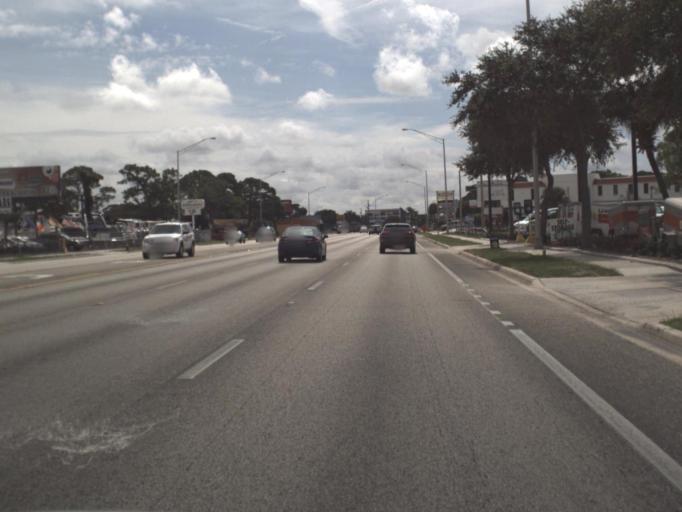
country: US
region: Florida
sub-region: Manatee County
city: Whitfield
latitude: 27.4014
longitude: -82.5657
